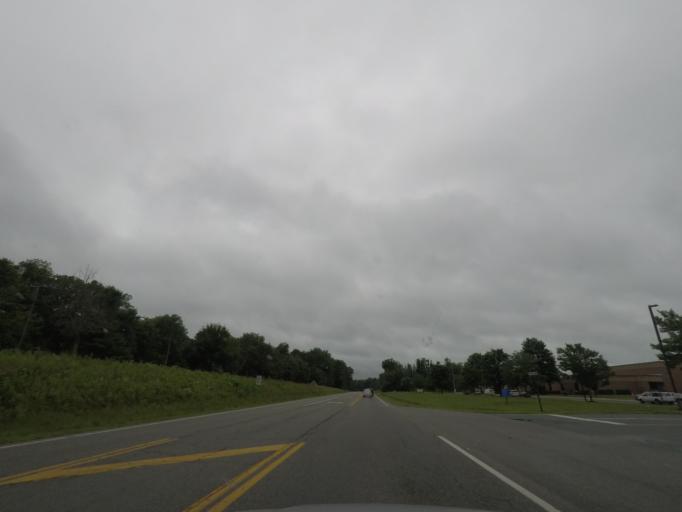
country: US
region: Virginia
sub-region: Fluvanna County
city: Palmyra
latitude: 37.8124
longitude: -78.2433
